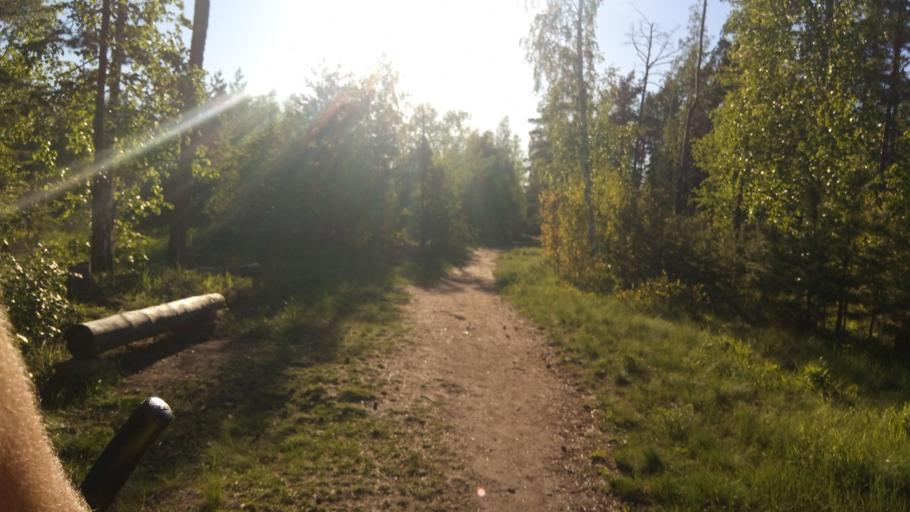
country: RU
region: Chelyabinsk
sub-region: Gorod Chelyabinsk
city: Chelyabinsk
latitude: 55.1260
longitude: 61.3445
